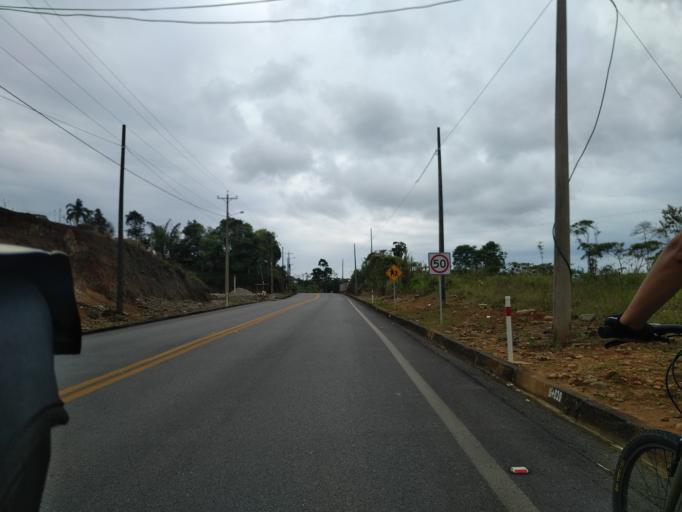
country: EC
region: Pastaza
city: Puyo
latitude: -1.3170
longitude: -77.8884
